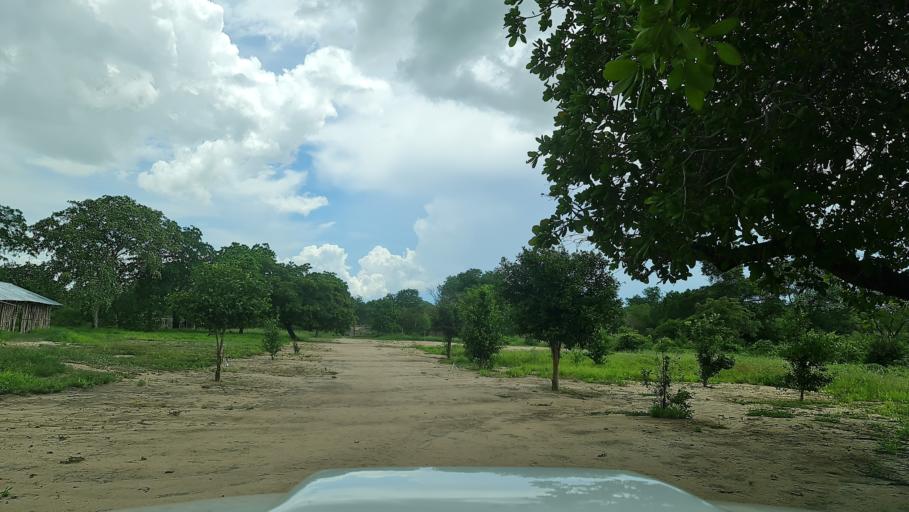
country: MZ
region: Nampula
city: Ilha de Mocambique
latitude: -15.4990
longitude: 40.1594
